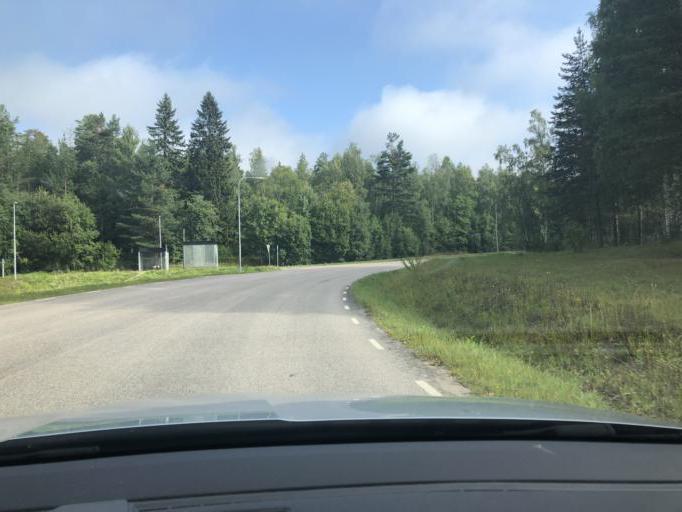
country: SE
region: Vaesternorrland
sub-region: Sundsvalls Kommun
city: Sundsvall
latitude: 62.4102
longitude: 17.3020
